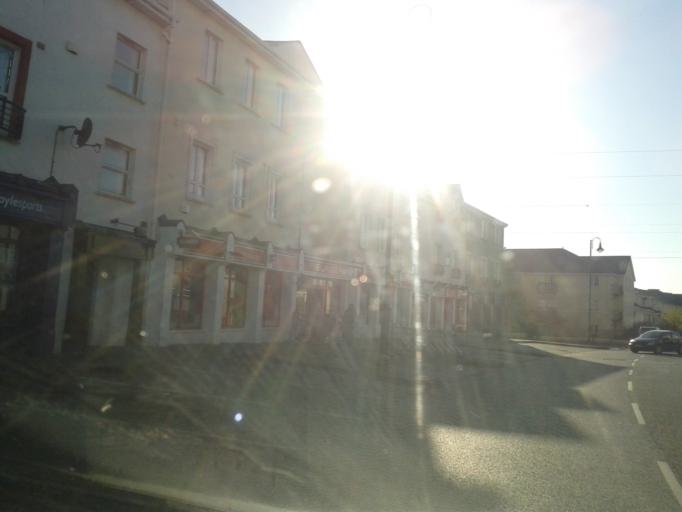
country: IE
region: Leinster
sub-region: Fingal County
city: Swords
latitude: 53.4710
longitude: -6.2320
